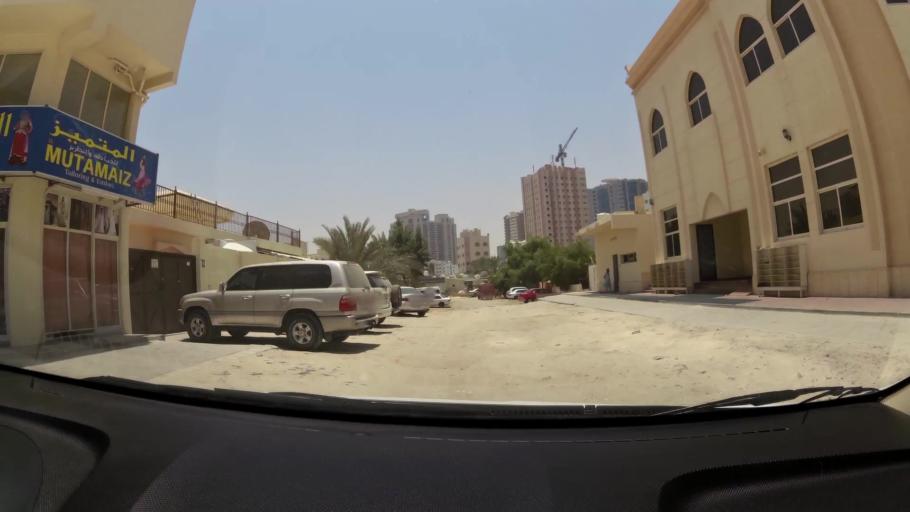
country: AE
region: Ajman
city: Ajman
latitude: 25.3961
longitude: 55.4337
